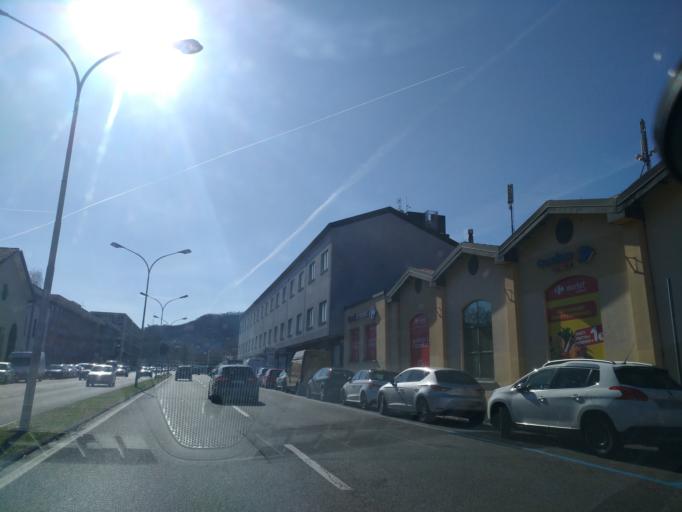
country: IT
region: Lombardy
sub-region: Provincia di Como
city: Como
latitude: 45.8054
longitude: 9.0795
